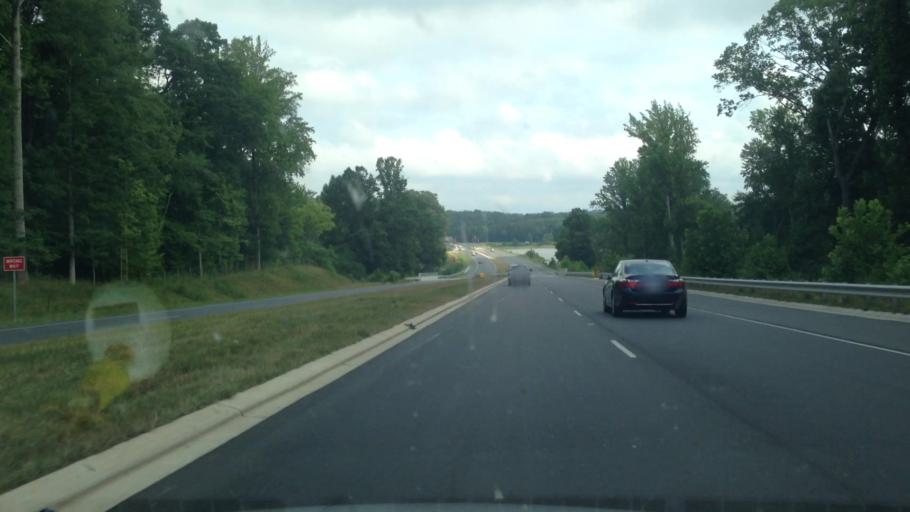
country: US
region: North Carolina
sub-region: Guilford County
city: Summerfield
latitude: 36.1668
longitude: -79.8787
